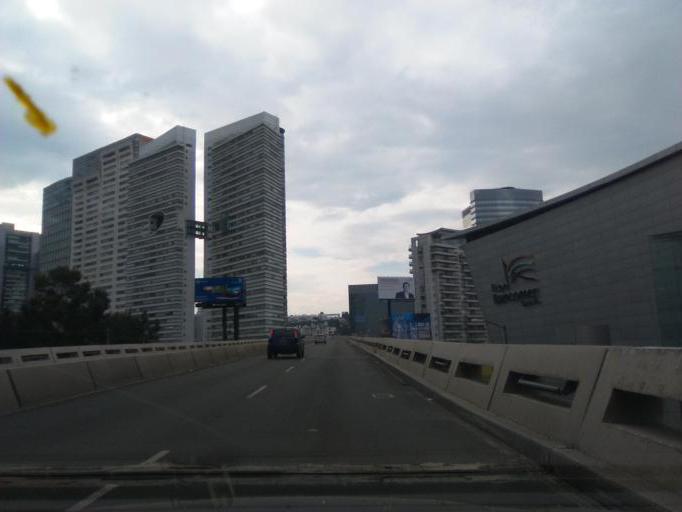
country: MX
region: Mexico City
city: Col. Bosques de las Lomas
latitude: 19.3625
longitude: -99.2637
